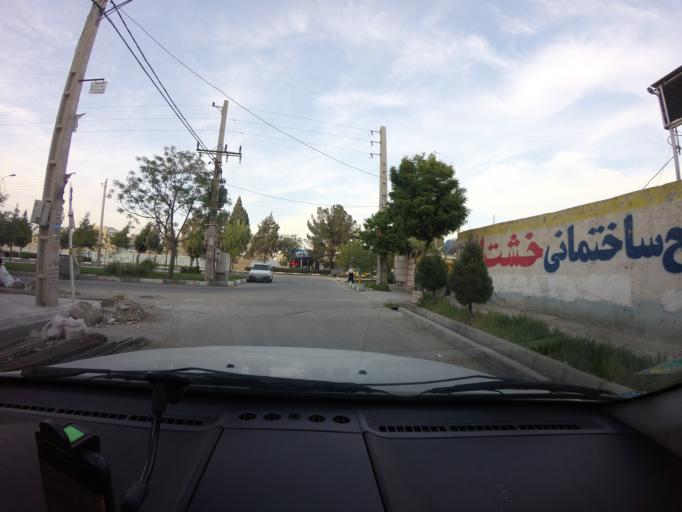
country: IR
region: Tehran
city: Eslamshahr
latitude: 35.5339
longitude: 51.2163
